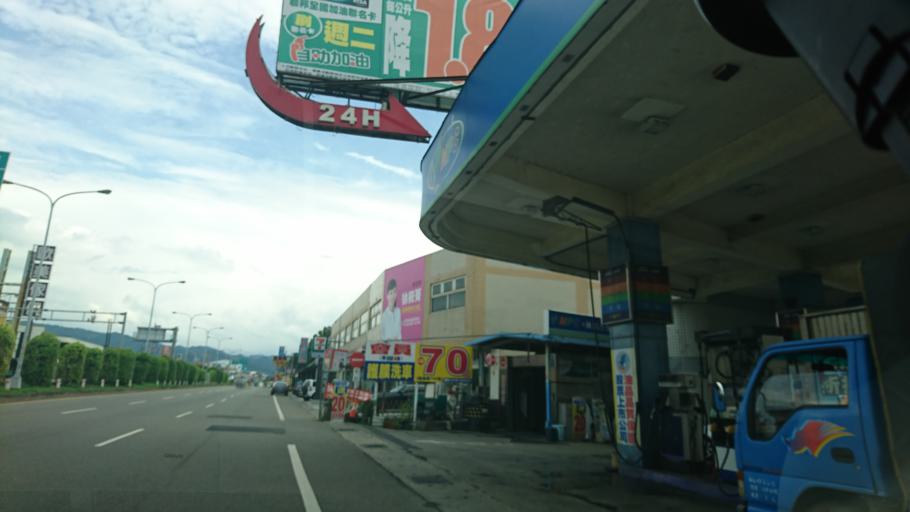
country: TW
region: Taiwan
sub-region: Miaoli
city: Miaoli
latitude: 24.5325
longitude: 120.8173
